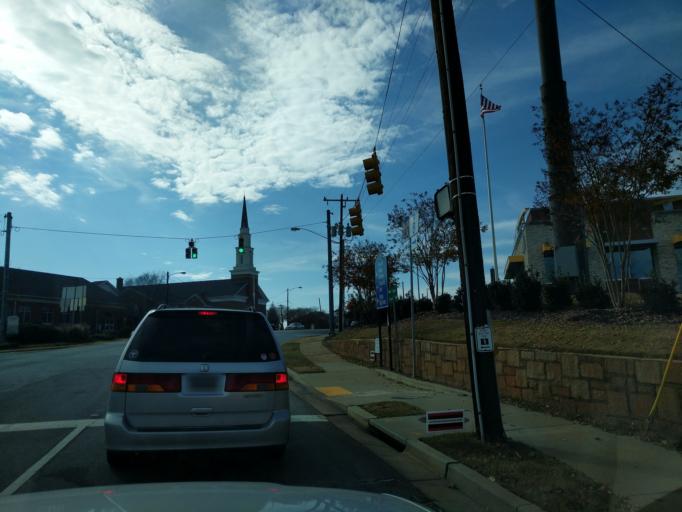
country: US
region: South Carolina
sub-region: Pickens County
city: Pickens
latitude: 34.8850
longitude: -82.7040
